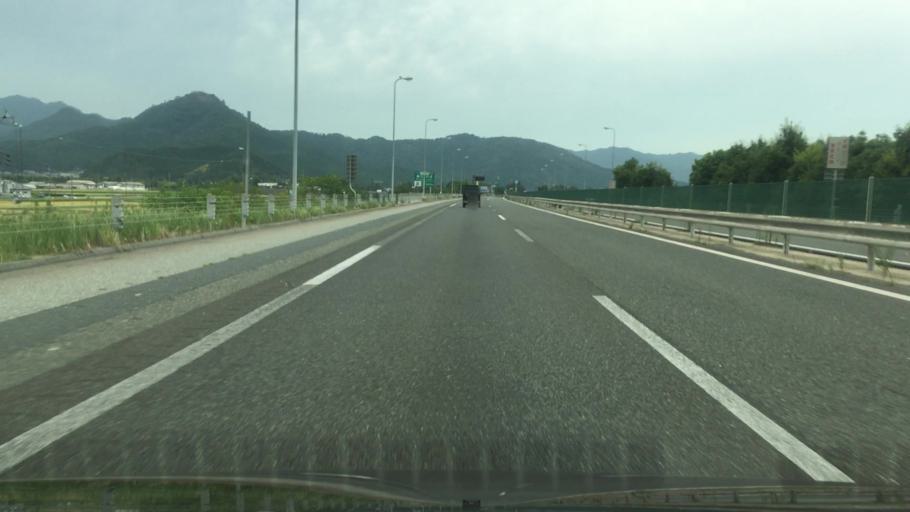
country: JP
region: Hyogo
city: Sasayama
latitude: 35.1572
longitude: 135.1207
